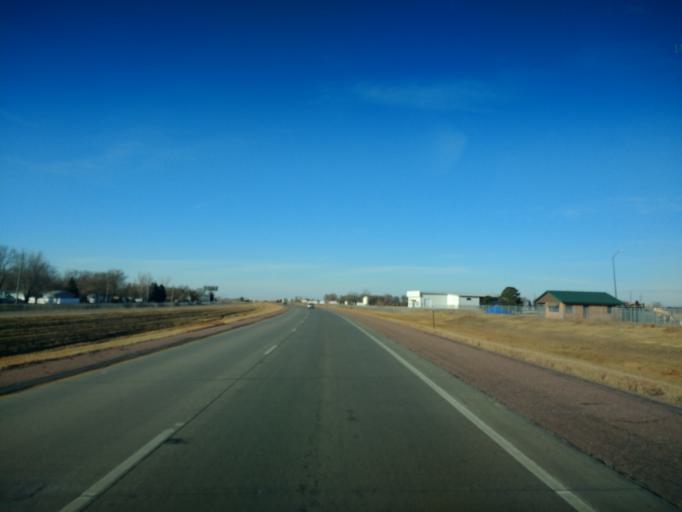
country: US
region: South Dakota
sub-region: Union County
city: North Sioux City
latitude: 42.5407
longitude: -96.5010
